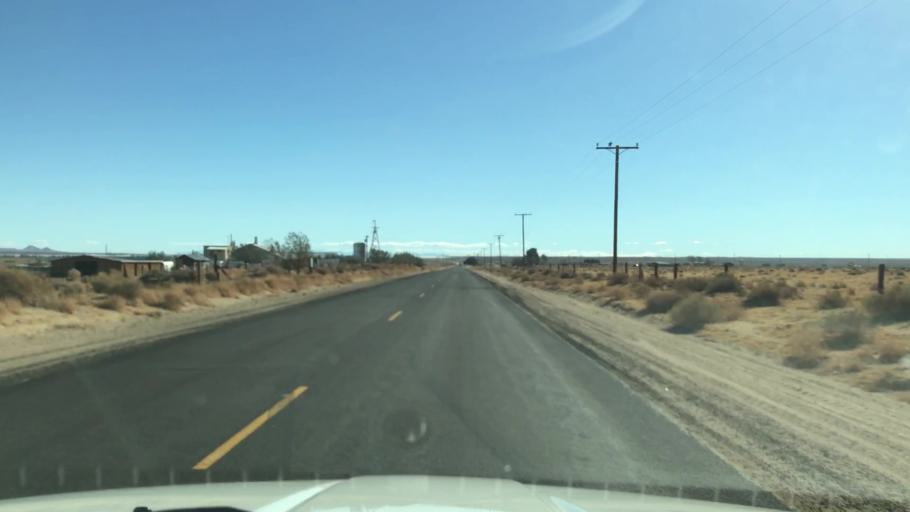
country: US
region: California
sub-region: Kern County
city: California City
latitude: 35.2926
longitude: -117.9859
